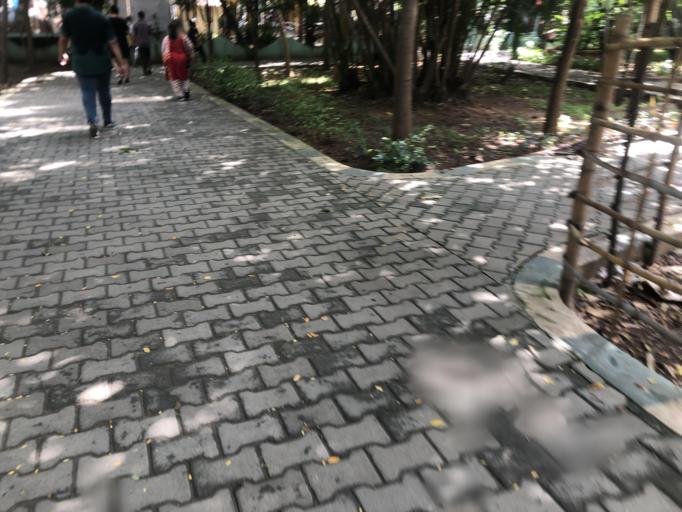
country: IN
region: Tamil Nadu
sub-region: Chennai
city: Gandhi Nagar
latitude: 13.0370
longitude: 80.2634
